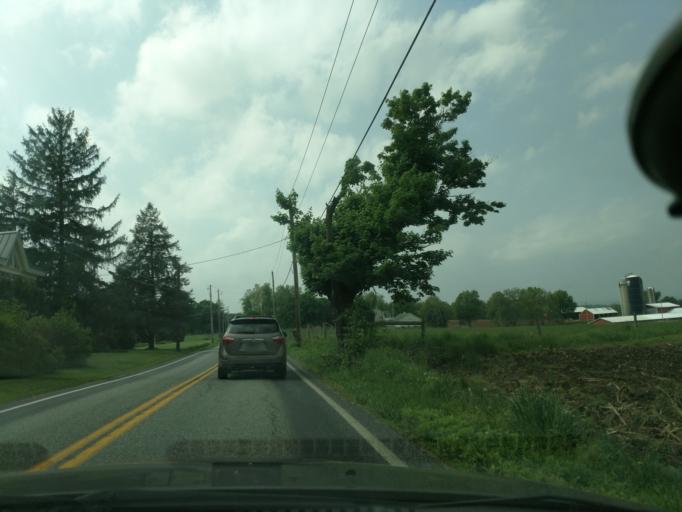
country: US
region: Pennsylvania
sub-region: Chester County
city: Spring City
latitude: 40.1602
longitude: -75.5838
